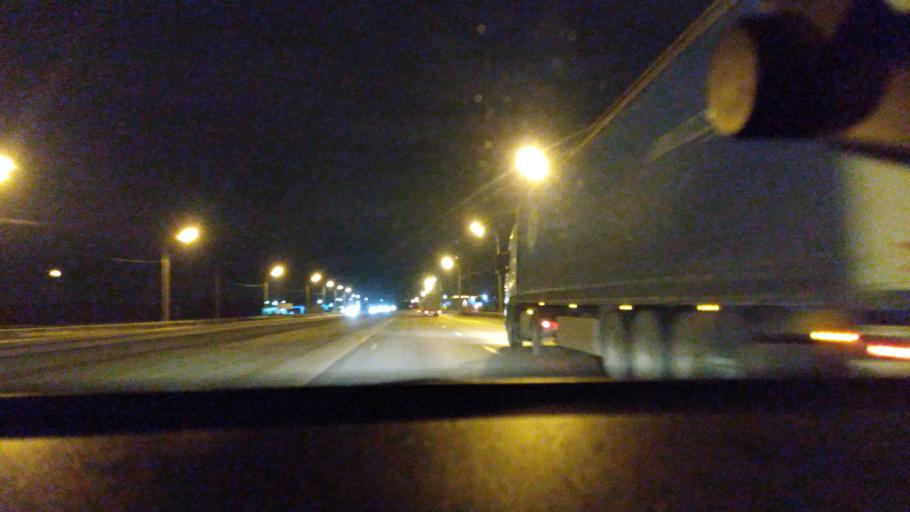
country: RU
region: Moskovskaya
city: Kolomna
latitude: 55.1215
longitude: 38.8167
